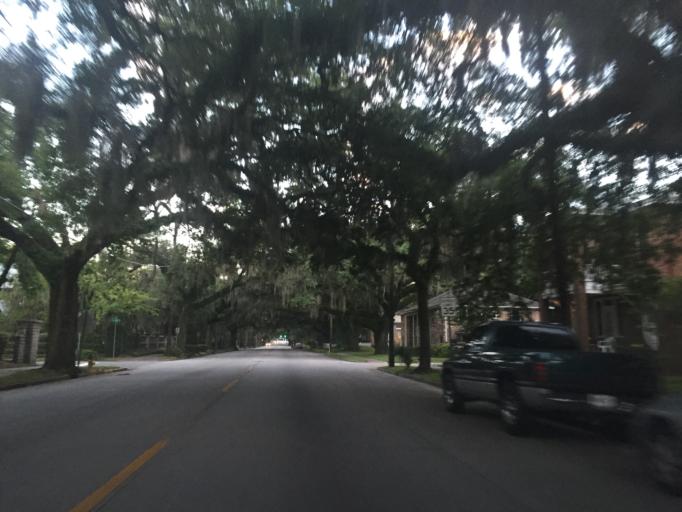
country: US
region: Georgia
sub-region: Chatham County
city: Savannah
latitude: 32.0484
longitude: -81.1037
